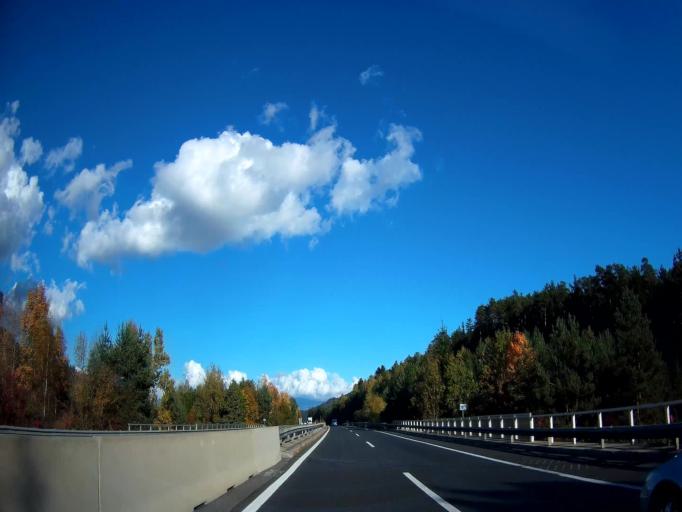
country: AT
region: Carinthia
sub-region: Politischer Bezirk Volkermarkt
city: Voelkermarkt
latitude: 46.6830
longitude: 14.6790
